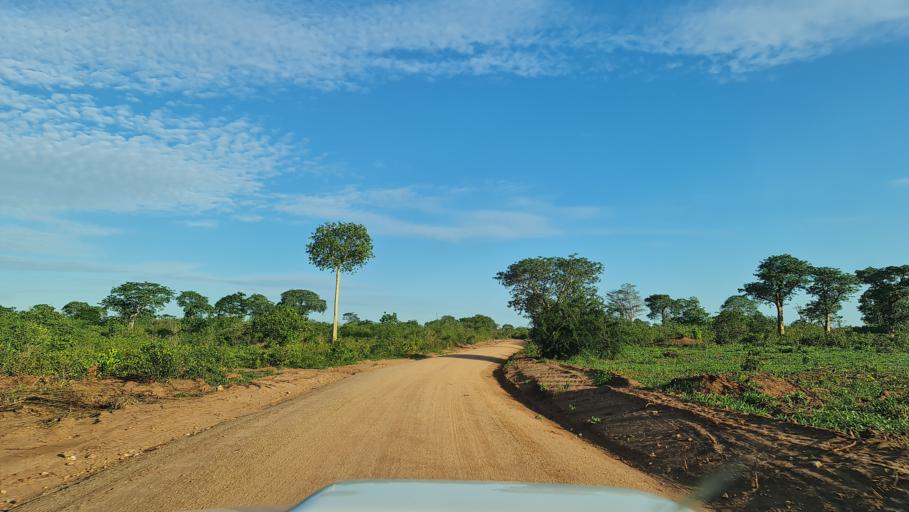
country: MZ
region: Nampula
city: Nacala
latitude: -14.6818
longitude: 40.2979
